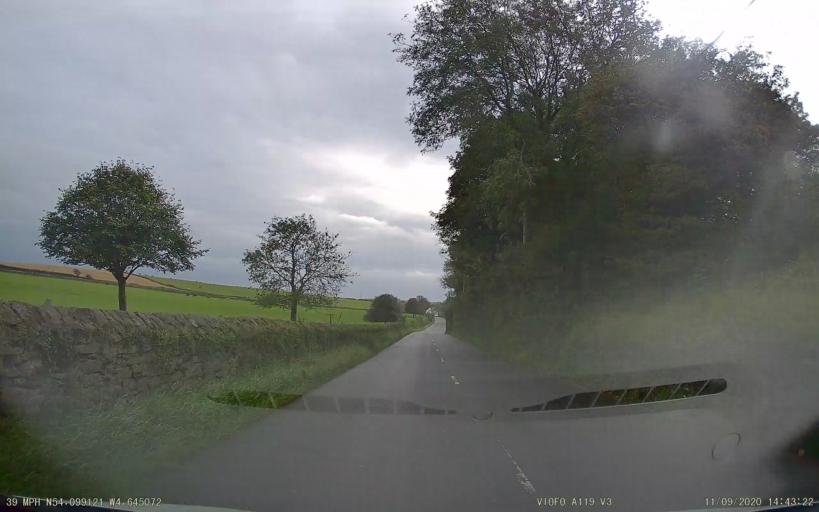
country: IM
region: Castletown
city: Castletown
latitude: 54.0991
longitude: -4.6453
